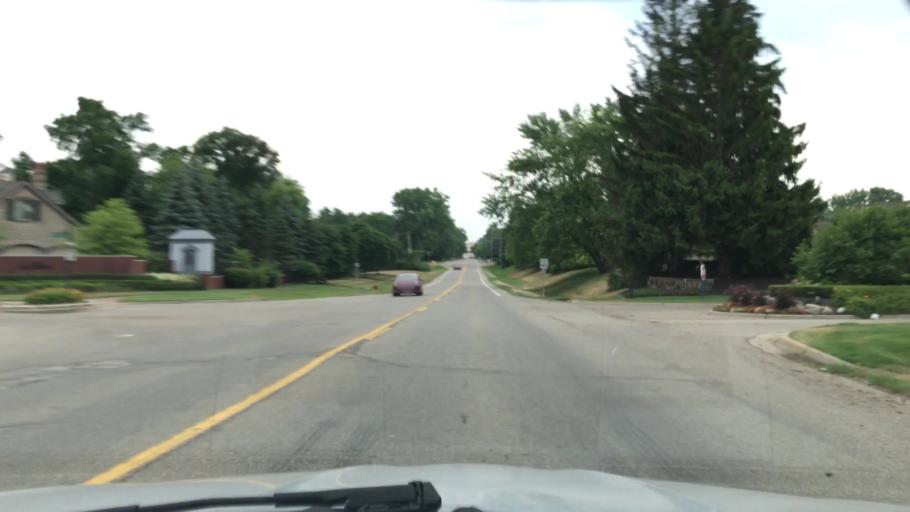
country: US
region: Michigan
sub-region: Wayne County
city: Northville
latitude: 42.4181
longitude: -83.5115
